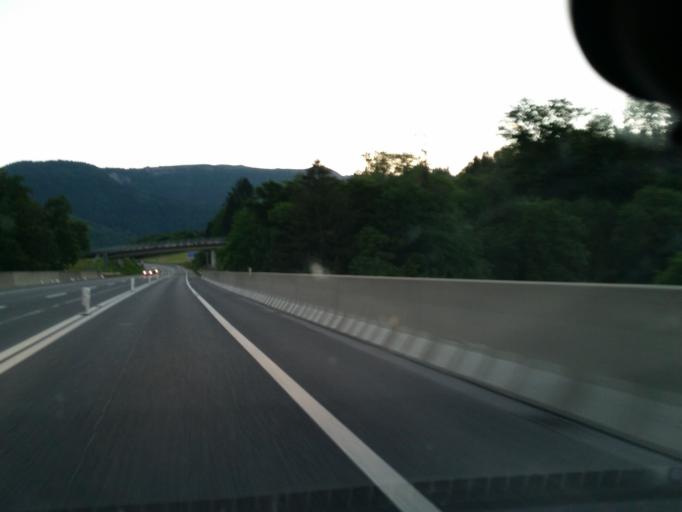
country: CH
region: Vaud
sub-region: Jura-Nord vaudois District
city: Vallorbe
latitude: 46.7260
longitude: 6.4101
